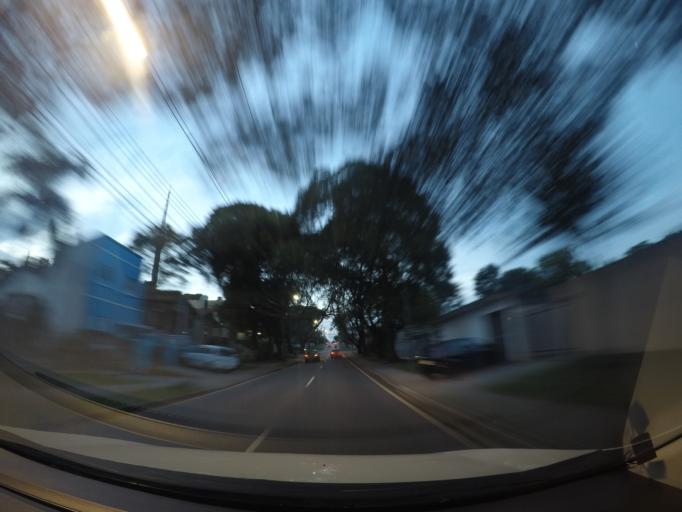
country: BR
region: Parana
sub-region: Curitiba
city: Curitiba
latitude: -25.4190
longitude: -49.2867
